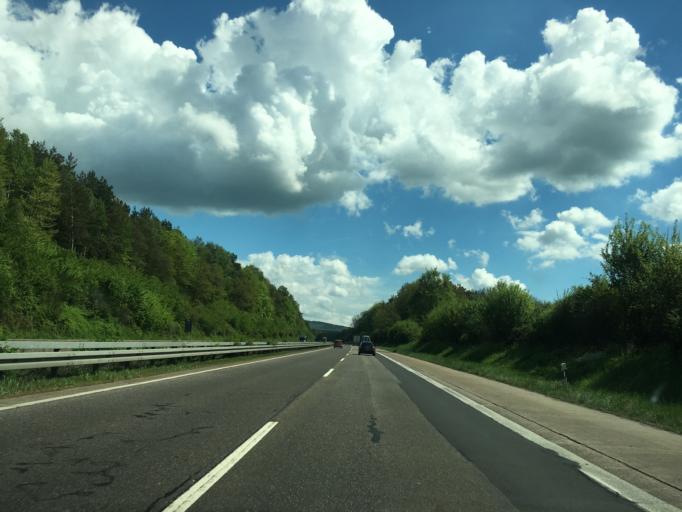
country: DE
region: Hesse
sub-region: Regierungsbezirk Kassel
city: Eichenzell
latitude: 50.4610
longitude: 9.7219
